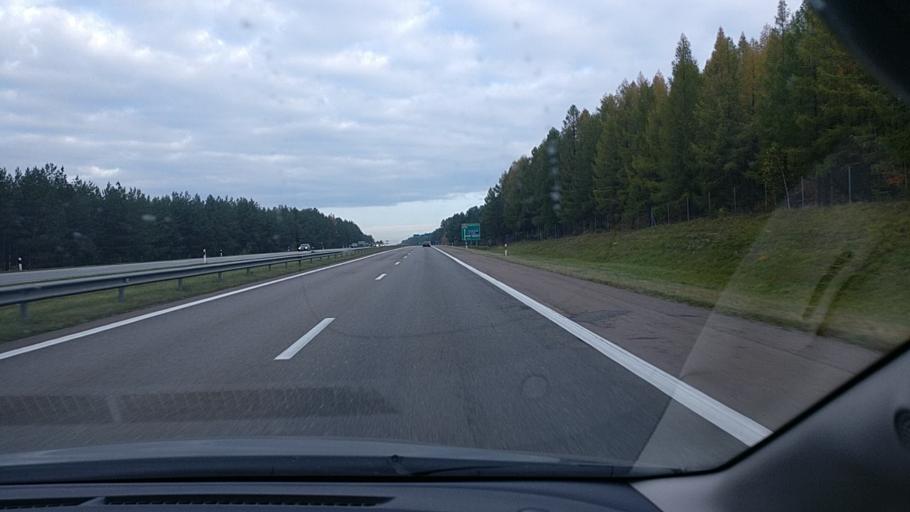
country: LT
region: Vilnius County
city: Ukmerge
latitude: 55.2628
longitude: 24.8139
